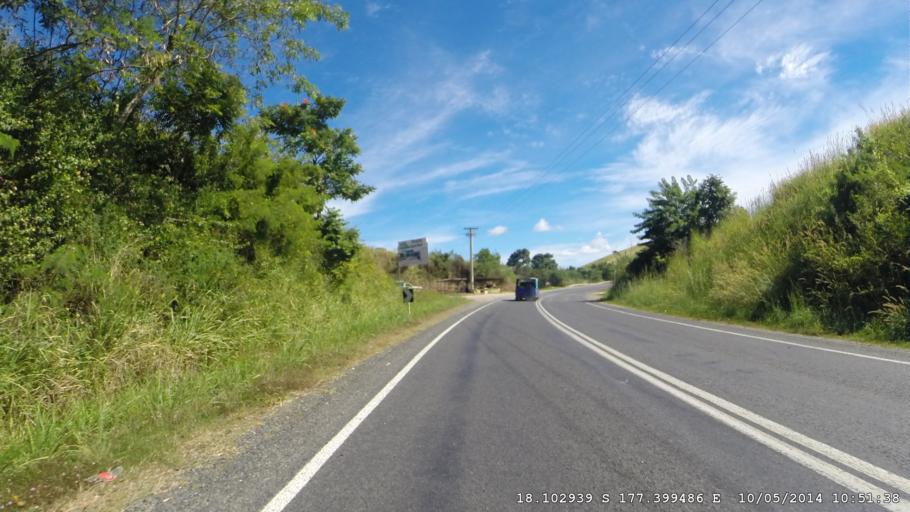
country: FJ
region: Western
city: Nadi
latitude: -18.1029
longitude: 177.3995
